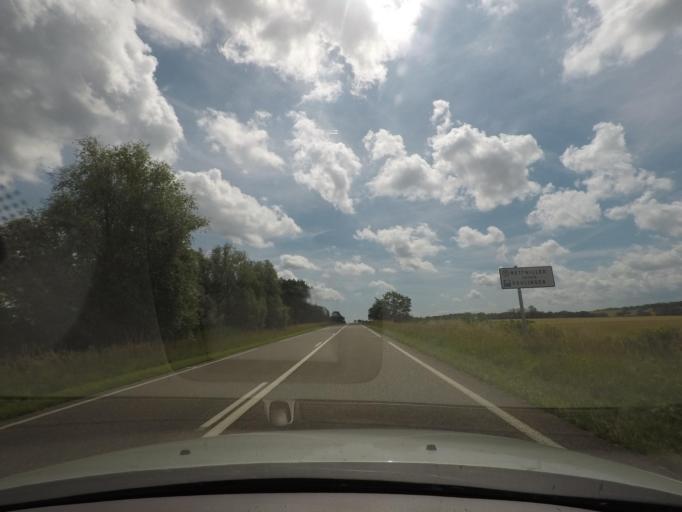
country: FR
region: Alsace
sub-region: Departement du Bas-Rhin
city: Drulingen
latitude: 48.8847
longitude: 7.1448
